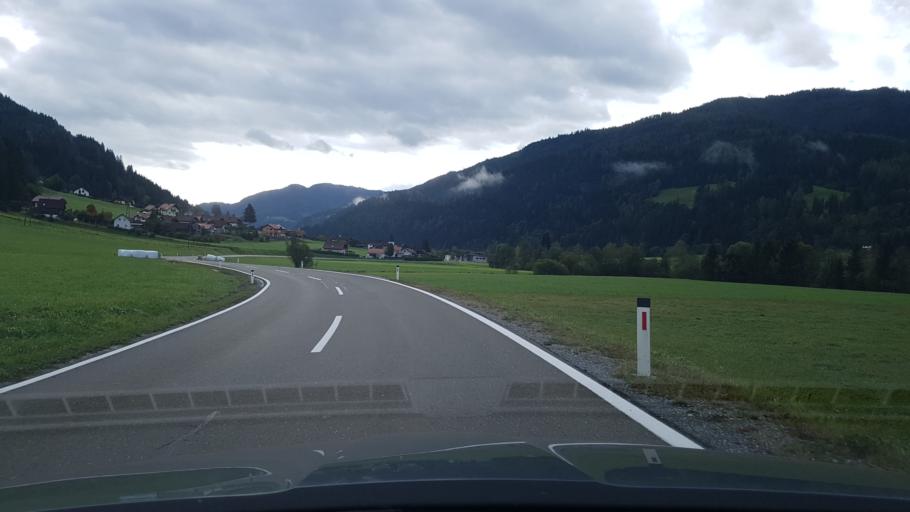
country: AT
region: Styria
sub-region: Politischer Bezirk Murau
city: Winklern bei Oberwolz
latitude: 47.1713
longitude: 14.2357
